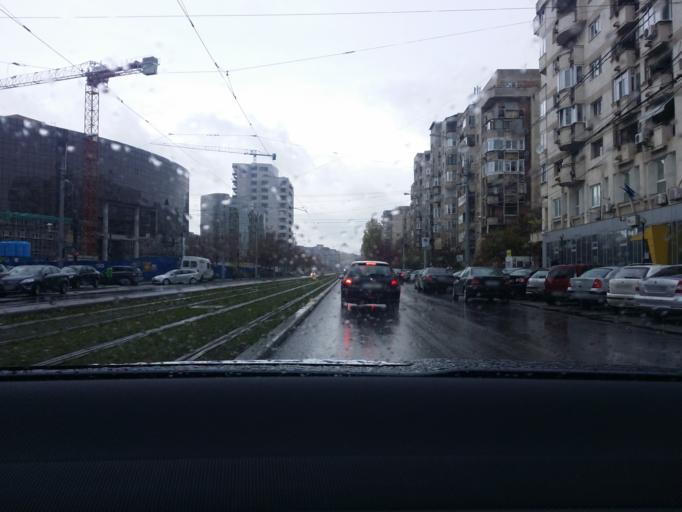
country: RO
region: Prahova
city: Ploiesti
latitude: 44.9460
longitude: 26.0184
